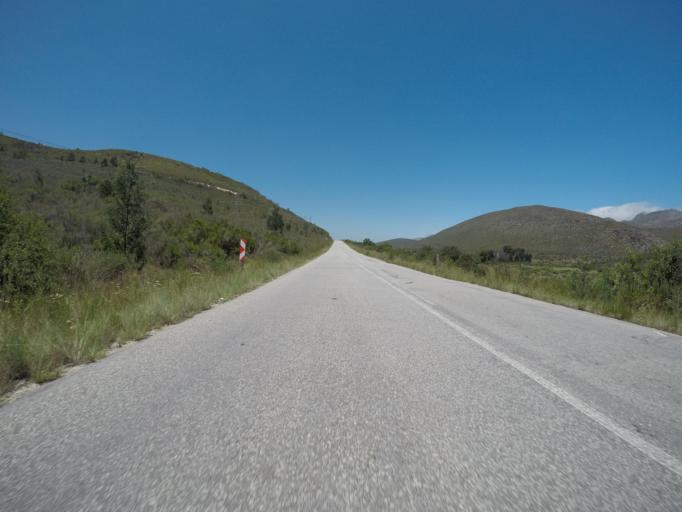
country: ZA
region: Eastern Cape
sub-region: Cacadu District Municipality
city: Kareedouw
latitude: -33.8652
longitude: 24.0109
